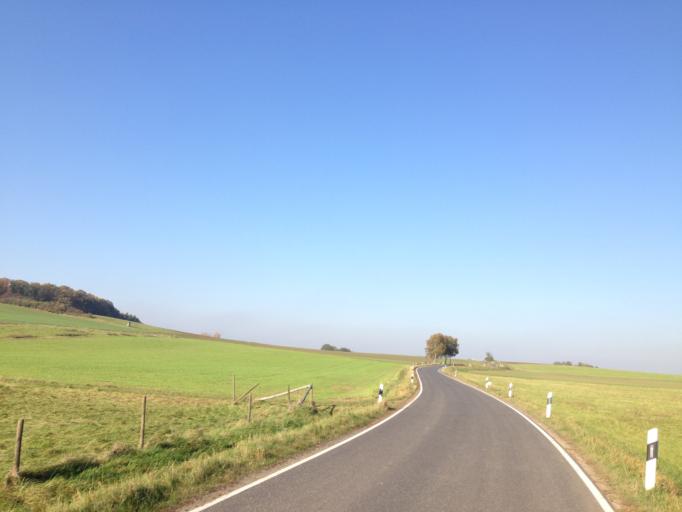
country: DE
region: Hesse
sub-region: Regierungsbezirk Giessen
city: Lich
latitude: 50.5608
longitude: 8.8079
